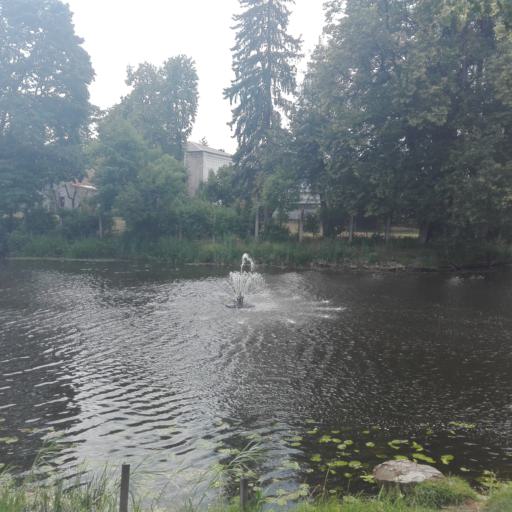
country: LT
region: Panevezys
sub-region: Birzai
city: Birzai
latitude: 56.2026
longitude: 24.7534
